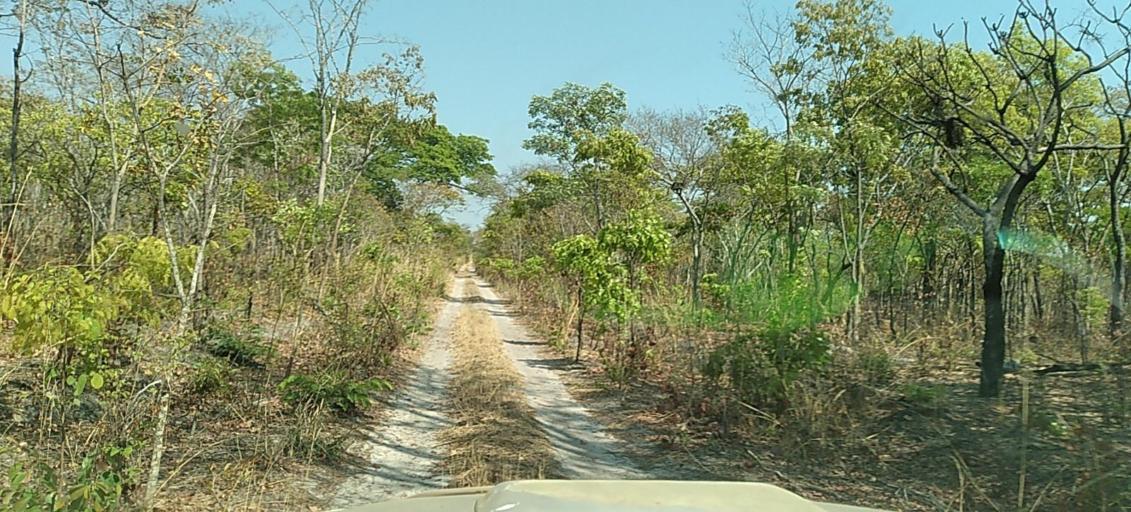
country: ZM
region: North-Western
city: Kalengwa
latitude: -13.3299
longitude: 24.8394
